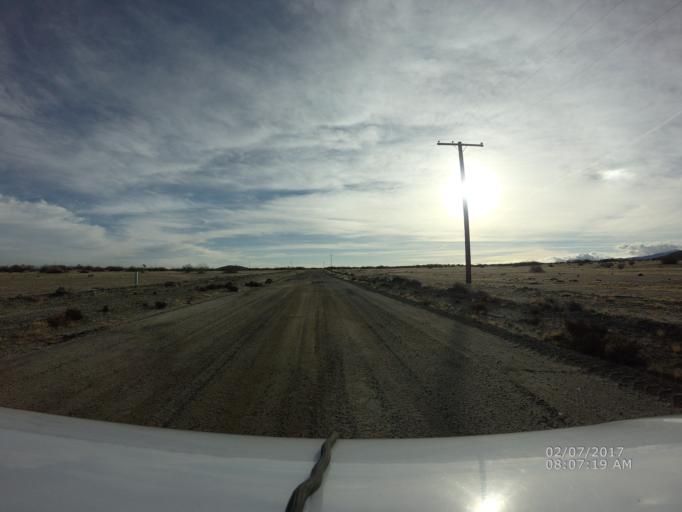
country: US
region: California
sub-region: Los Angeles County
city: Lake Los Angeles
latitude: 34.5724
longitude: -117.7238
